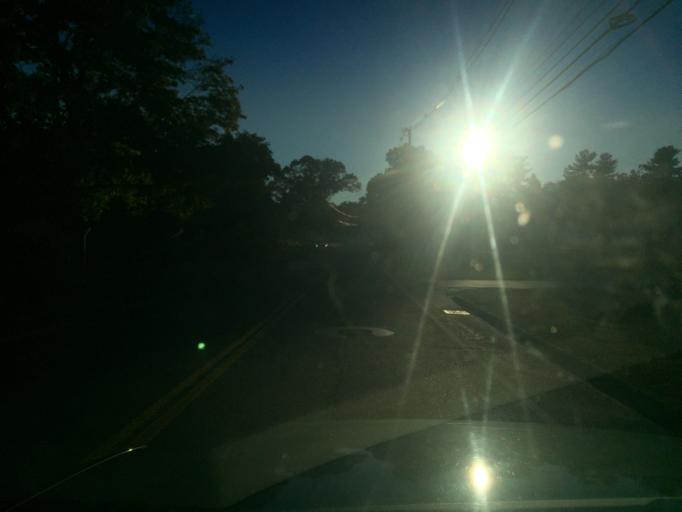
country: US
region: Massachusetts
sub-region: Middlesex County
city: Hudson
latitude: 42.3894
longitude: -71.5430
